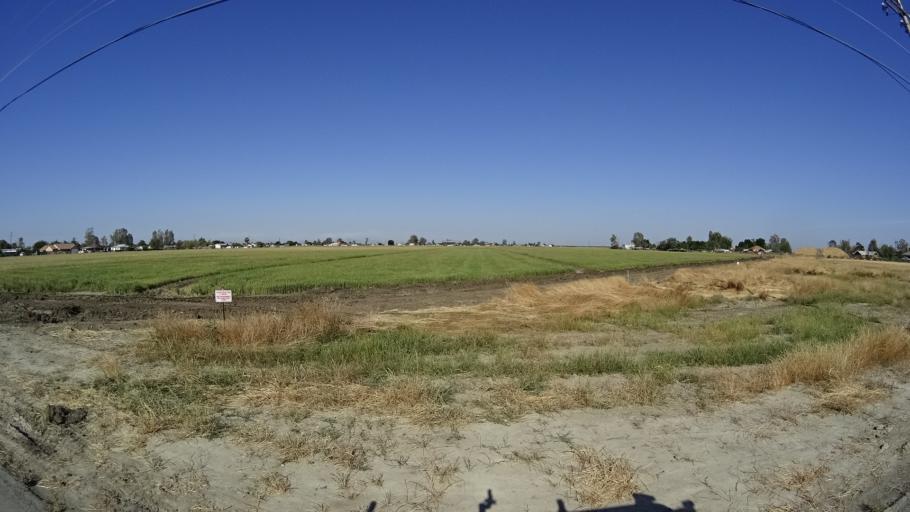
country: US
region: California
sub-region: Kings County
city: Corcoran
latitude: 36.1178
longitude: -119.5632
